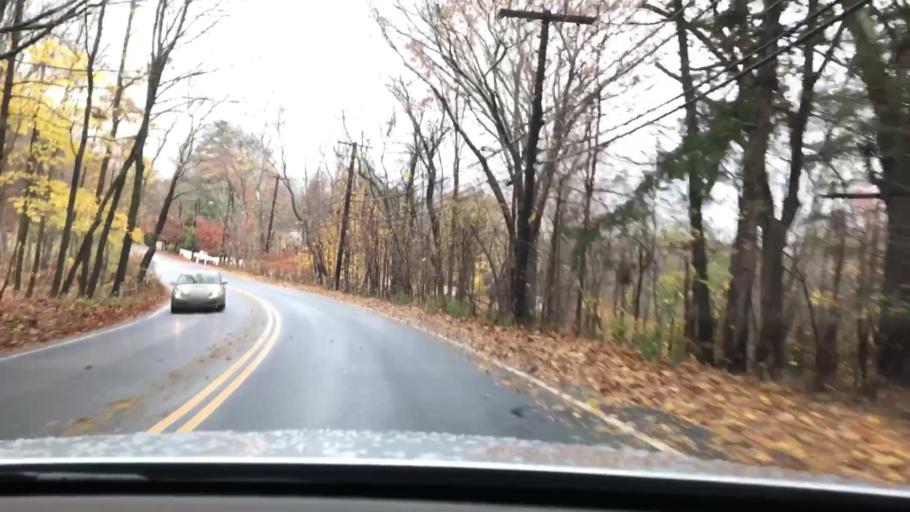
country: US
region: Massachusetts
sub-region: Norfolk County
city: Dedham
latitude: 42.2551
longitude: -71.1888
